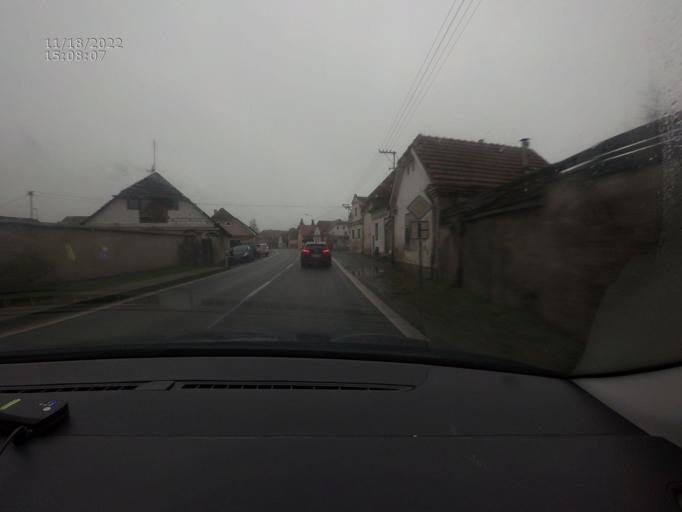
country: CZ
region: Jihocesky
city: Mirovice
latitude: 49.5164
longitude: 14.0900
